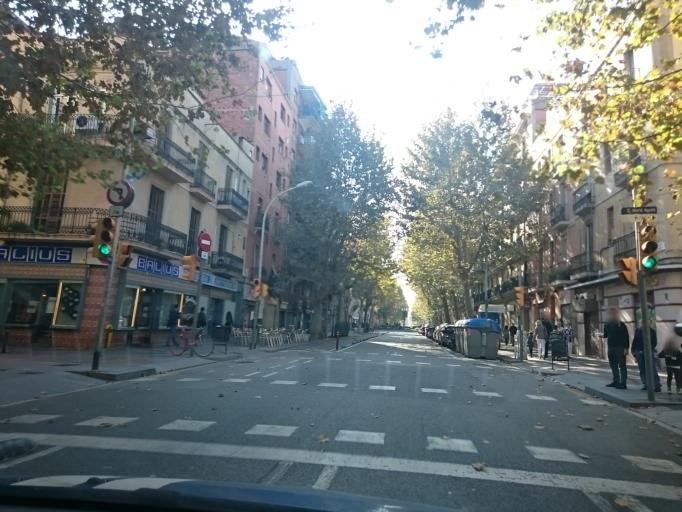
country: ES
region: Catalonia
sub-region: Provincia de Barcelona
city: Sant Marti
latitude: 41.4024
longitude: 2.2017
